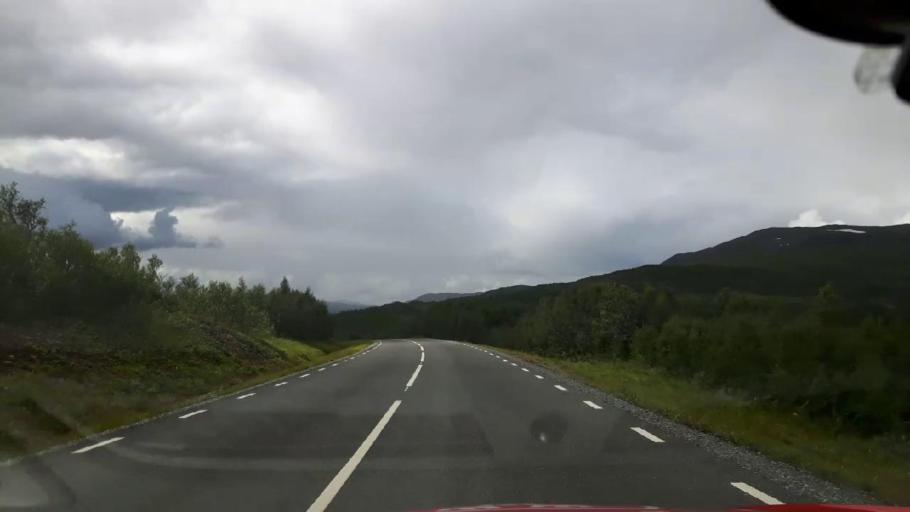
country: NO
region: Nordland
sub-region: Hattfjelldal
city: Hattfjelldal
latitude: 64.9883
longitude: 14.2166
